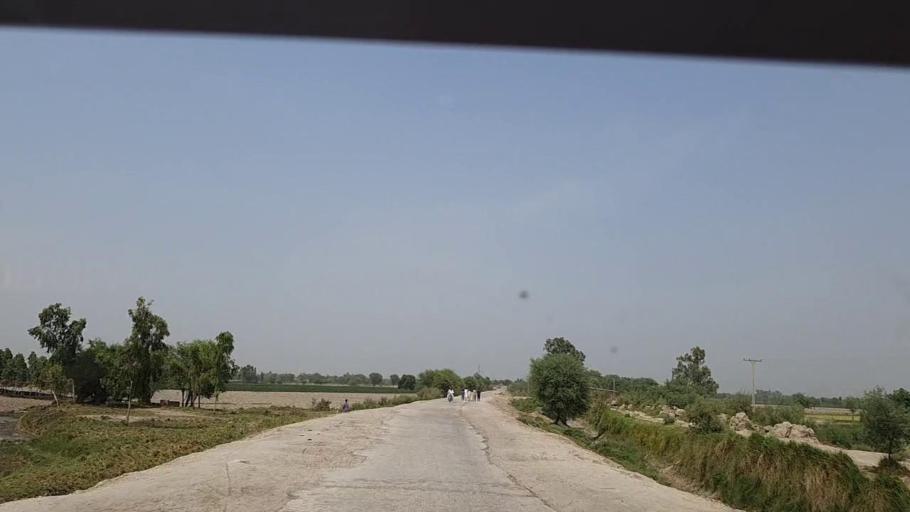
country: PK
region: Sindh
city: Khairpur Nathan Shah
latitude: 27.0767
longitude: 67.6532
